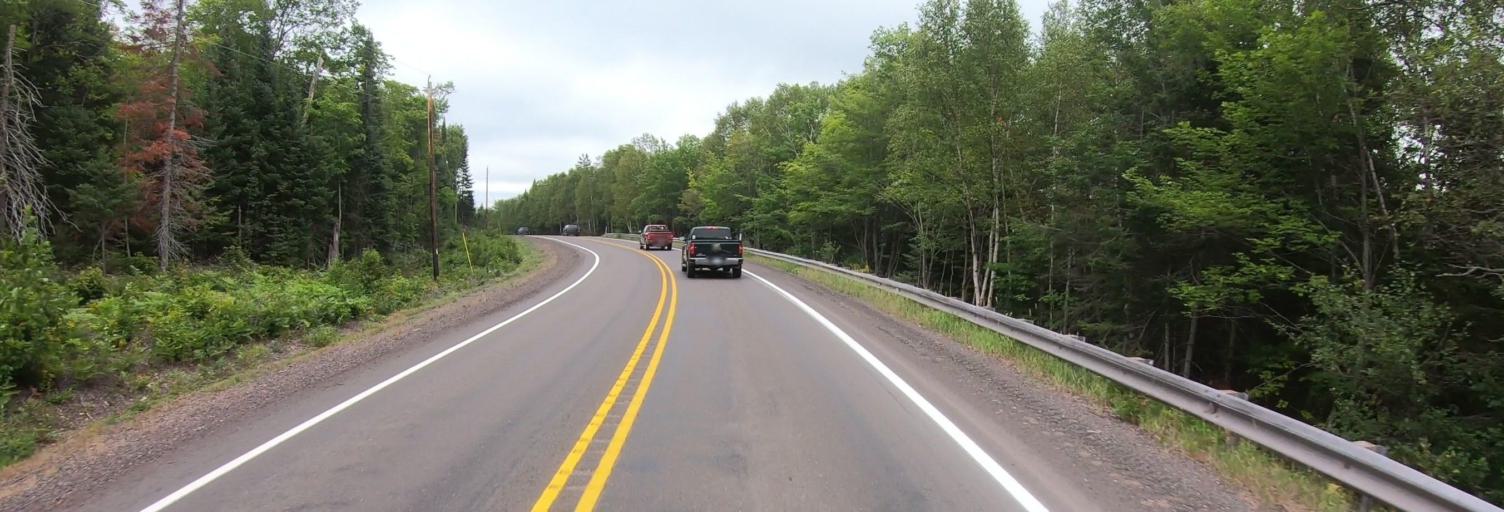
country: US
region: Michigan
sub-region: Keweenaw County
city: Eagle River
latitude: 47.4156
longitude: -88.1458
